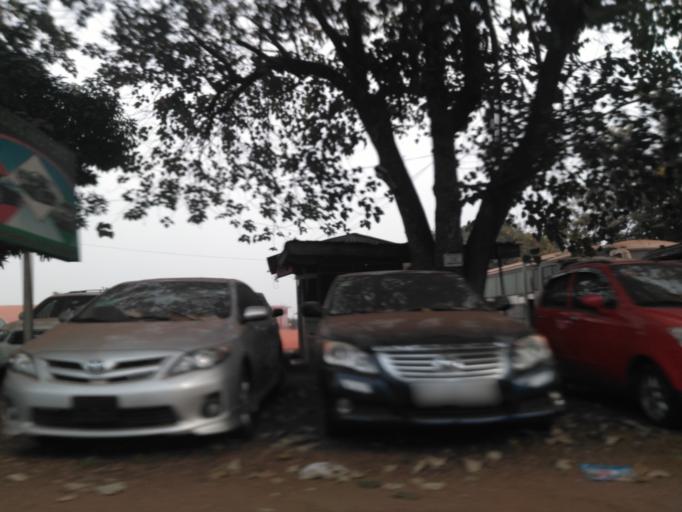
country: GH
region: Ashanti
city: Kumasi
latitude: 6.7094
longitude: -1.6339
